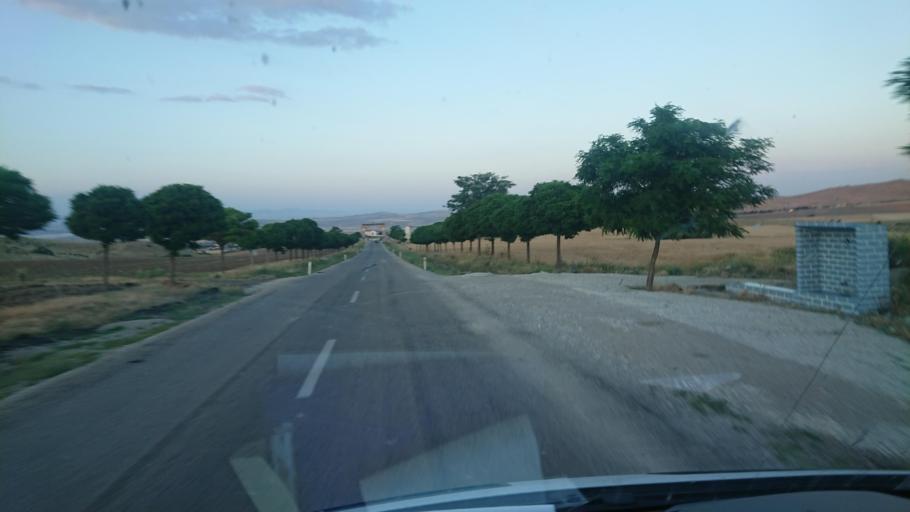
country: TR
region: Aksaray
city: Sariyahsi
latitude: 38.9696
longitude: 33.8171
